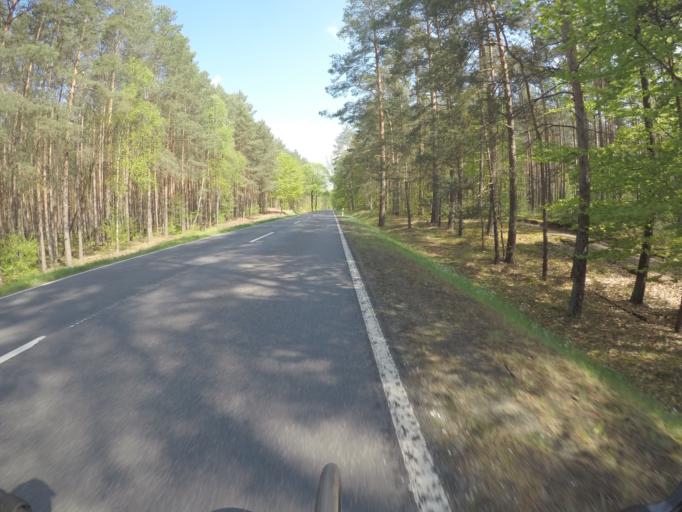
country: DE
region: Brandenburg
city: Marienwerder
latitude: 52.8013
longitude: 13.5517
